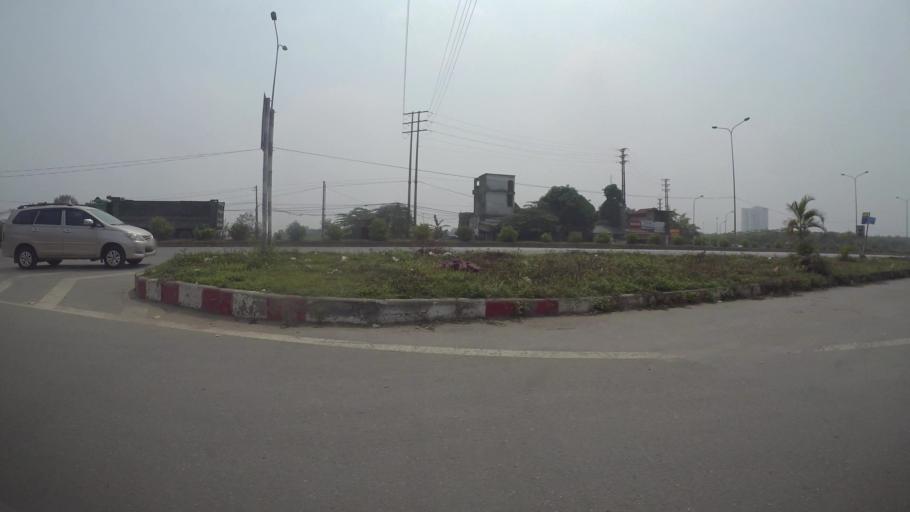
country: VN
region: Ha Noi
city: Lien Quan
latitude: 20.9939
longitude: 105.5236
